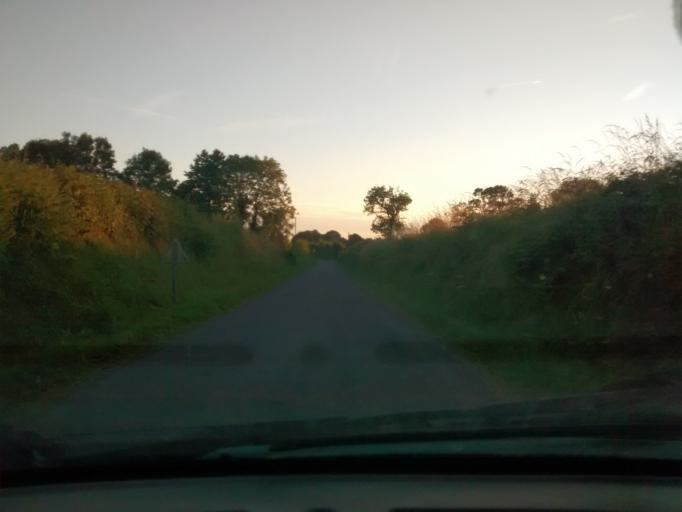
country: FR
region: Lower Normandy
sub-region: Departement de la Manche
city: Saint-Jean-des-Baisants
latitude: 49.1332
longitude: -1.0126
